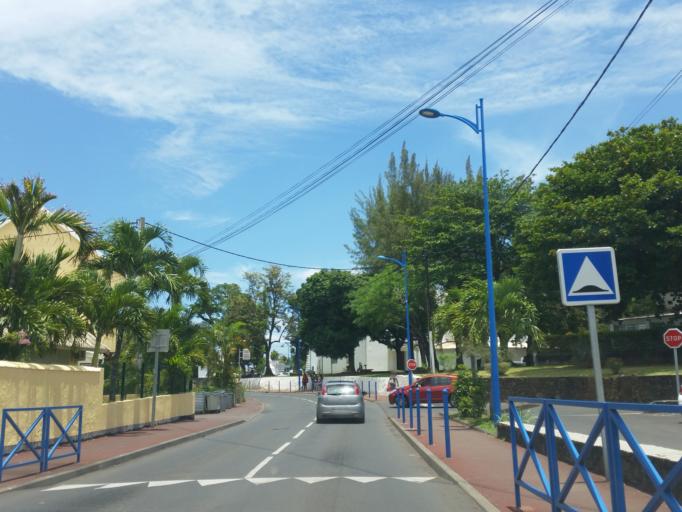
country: RE
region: Reunion
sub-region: Reunion
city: Sainte-Marie
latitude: -20.9144
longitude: 55.5101
